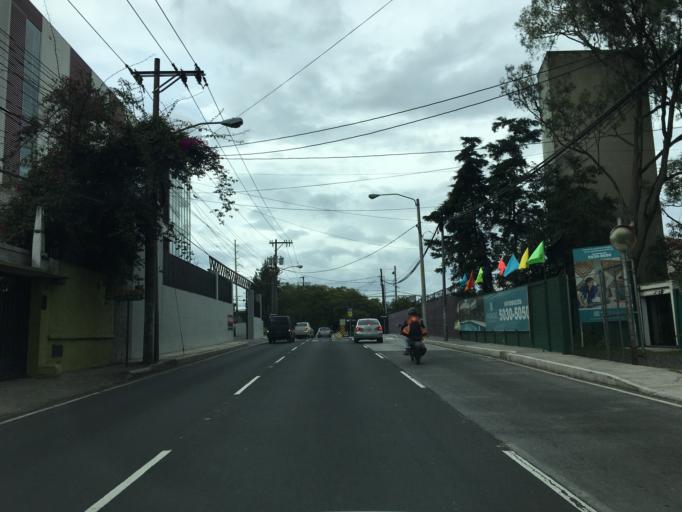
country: GT
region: Guatemala
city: Mixco
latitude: 14.5995
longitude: -90.5609
